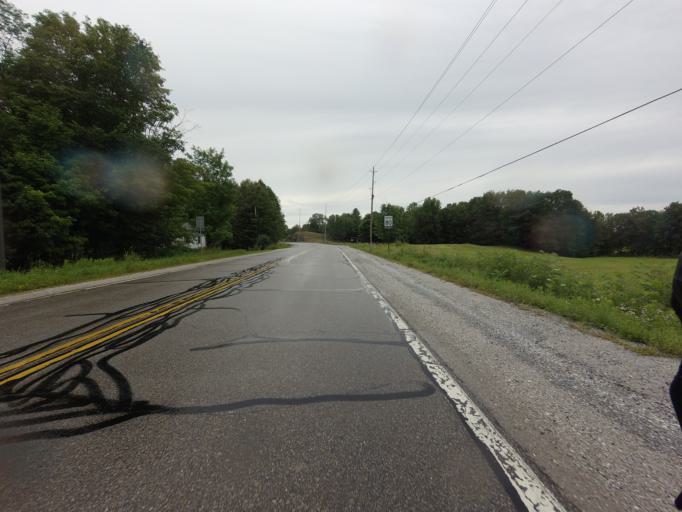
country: CA
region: Ontario
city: Perth
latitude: 44.9620
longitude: -76.3970
